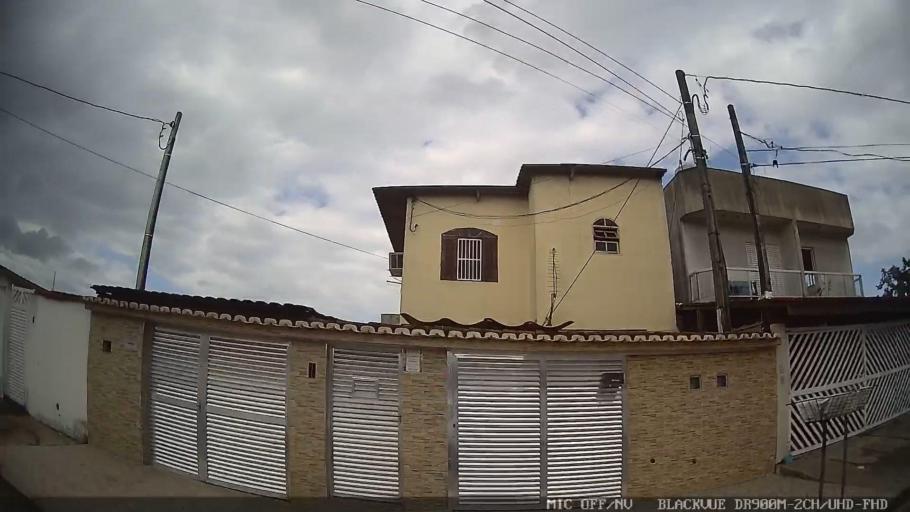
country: BR
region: Sao Paulo
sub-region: Guaruja
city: Guaruja
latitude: -23.9865
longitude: -46.2772
